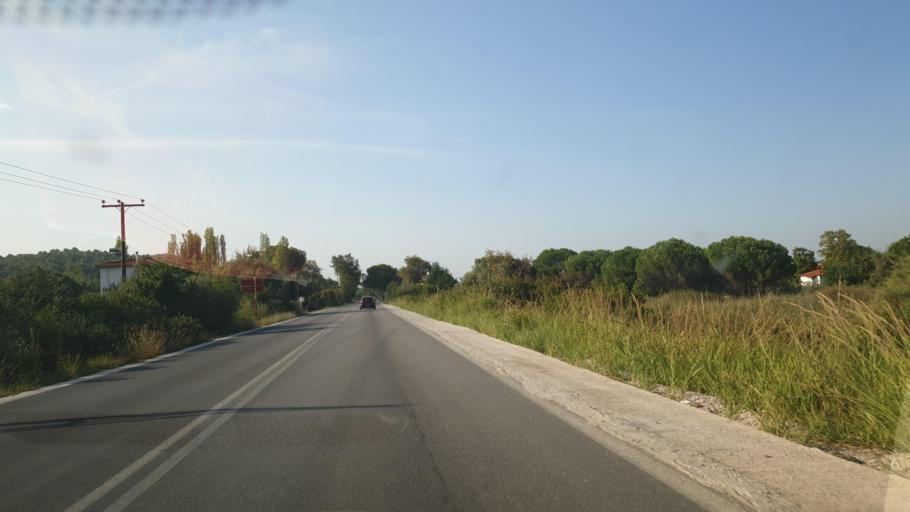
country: GR
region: Central Macedonia
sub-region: Nomos Chalkidikis
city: Agios Nikolaos
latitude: 40.1924
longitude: 23.7698
